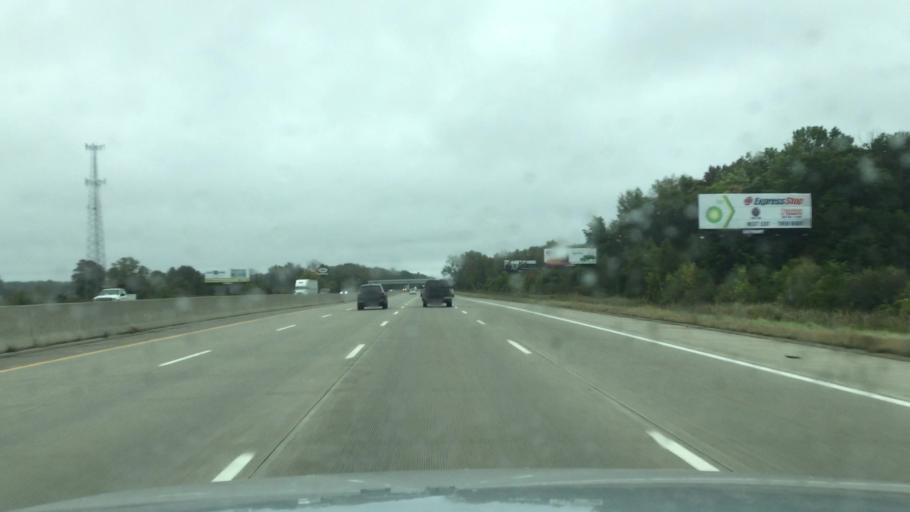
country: US
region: Michigan
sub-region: Saginaw County
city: Birch Run
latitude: 43.2981
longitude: -83.8252
